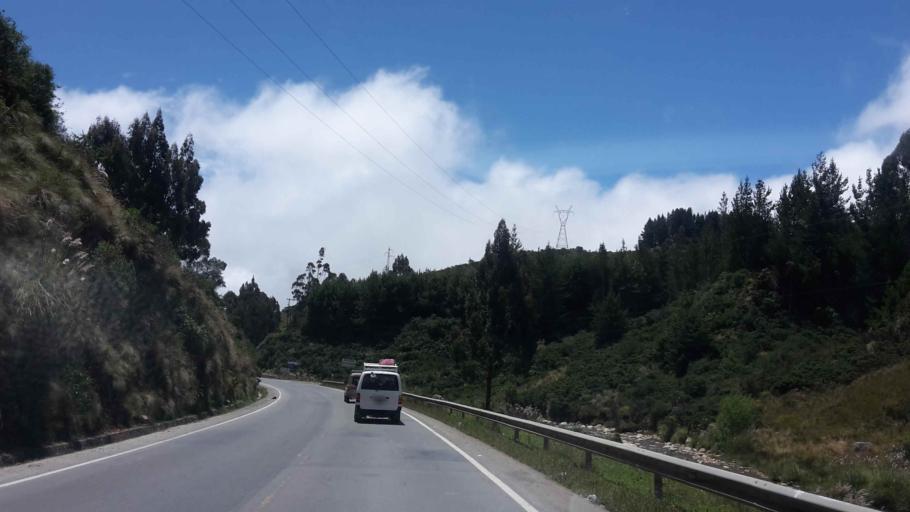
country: BO
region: Cochabamba
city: Colomi
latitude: -17.2698
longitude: -65.8791
